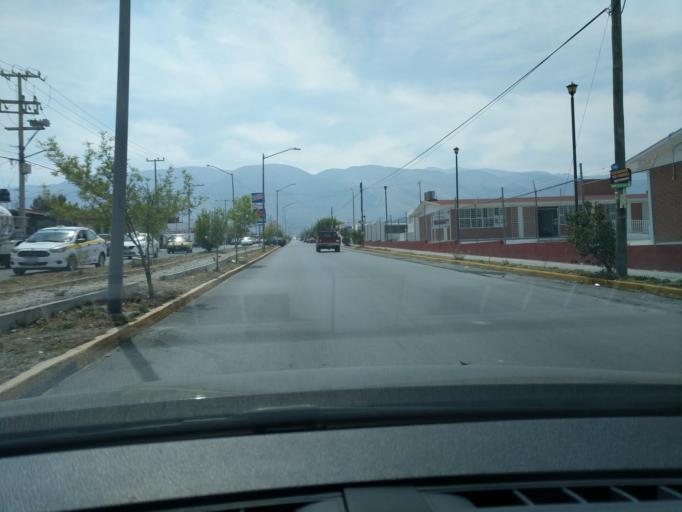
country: MX
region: Coahuila
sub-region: Arteaga
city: Arteaga
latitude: 25.4269
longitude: -100.9032
